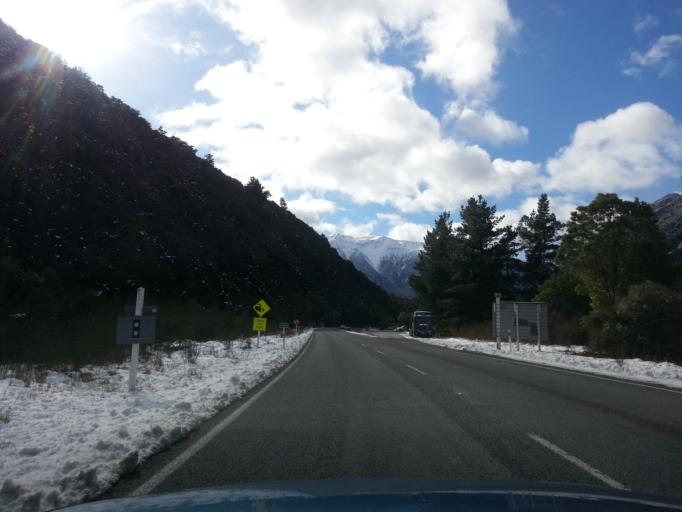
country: NZ
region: West Coast
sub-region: Grey District
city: Greymouth
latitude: -42.8450
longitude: 171.5599
